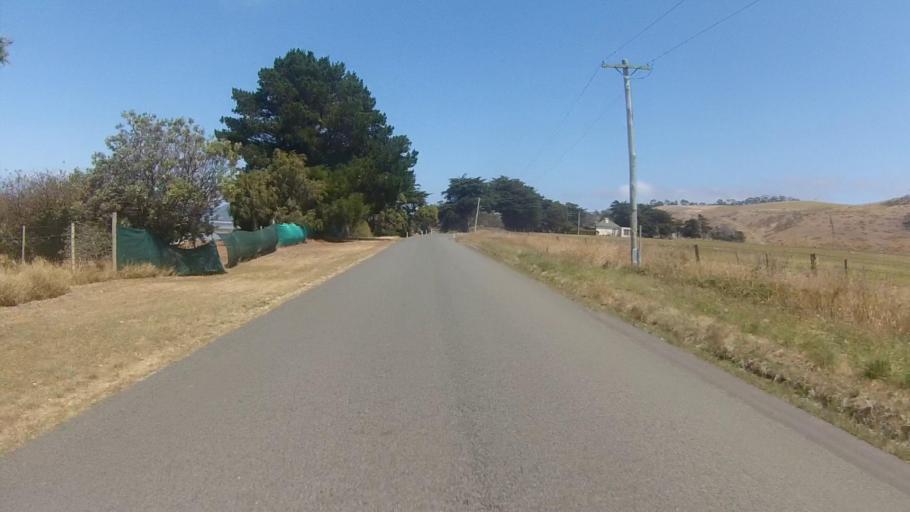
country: AU
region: Tasmania
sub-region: Sorell
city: Sorell
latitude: -42.8278
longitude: 147.8586
